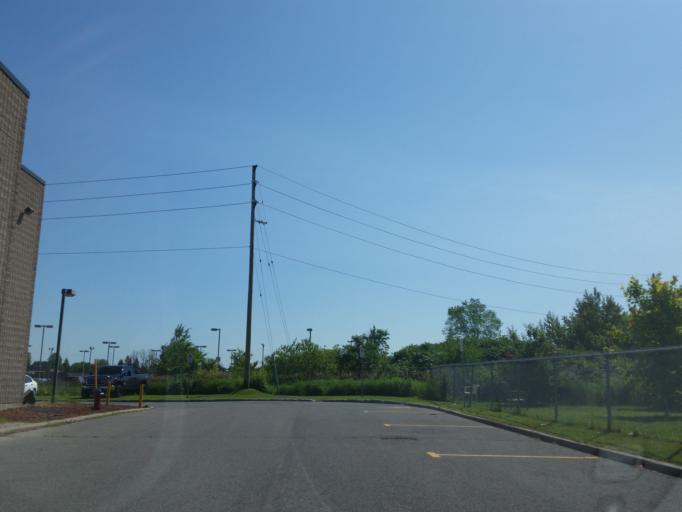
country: CA
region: Quebec
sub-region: Outaouais
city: Gatineau
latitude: 45.4635
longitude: -75.5485
